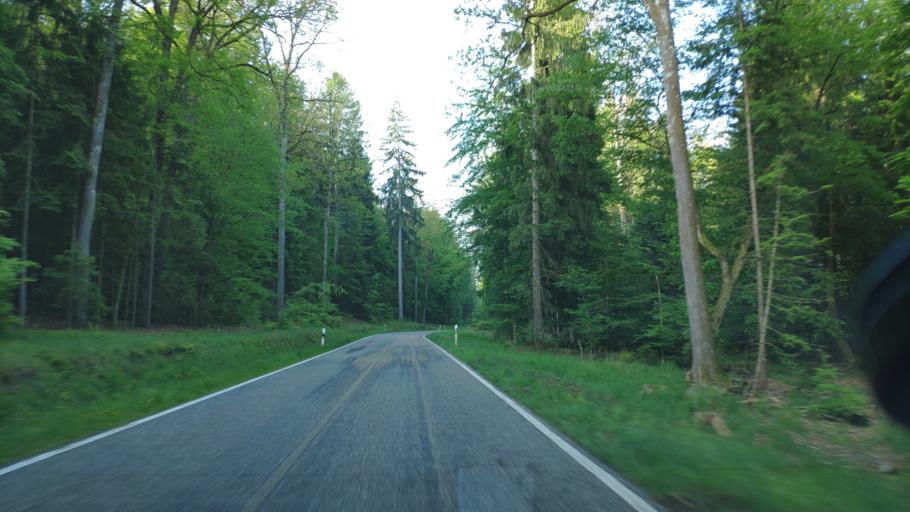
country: DE
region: Rheinland-Pfalz
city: Lemberg
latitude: 49.1559
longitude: 7.7123
